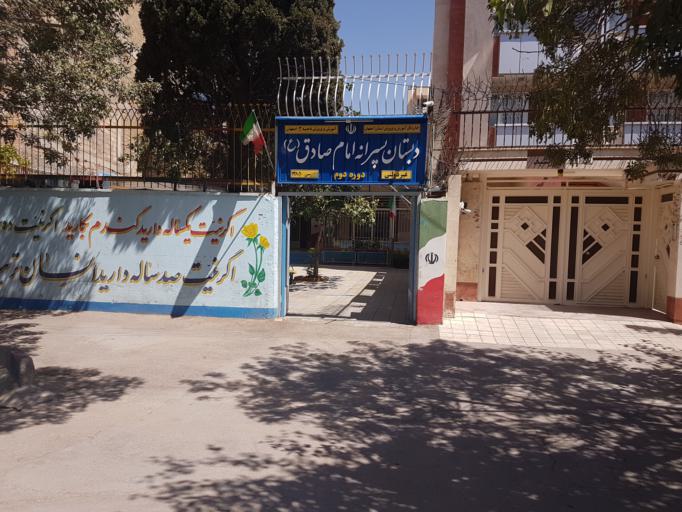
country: IR
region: Isfahan
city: Isfahan
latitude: 32.6331
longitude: 51.6569
